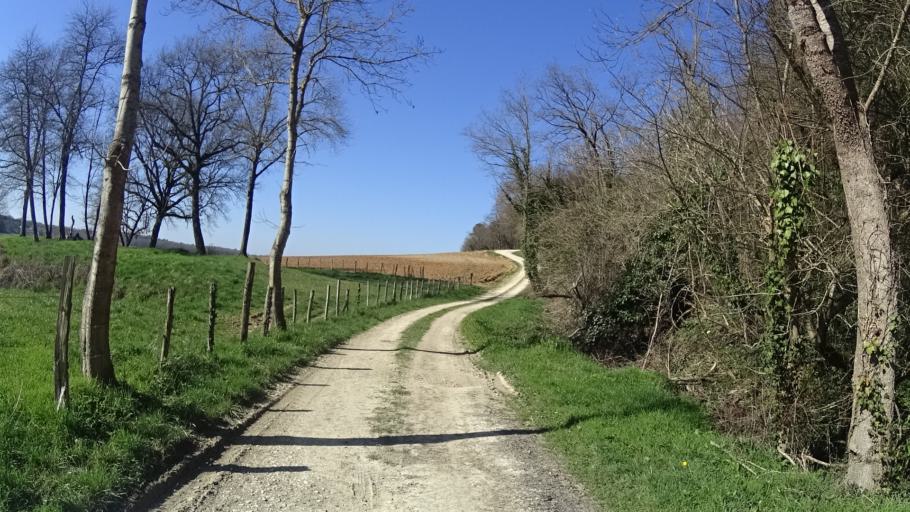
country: FR
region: Aquitaine
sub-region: Departement de la Dordogne
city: Riberac
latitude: 45.2133
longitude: 0.3293
